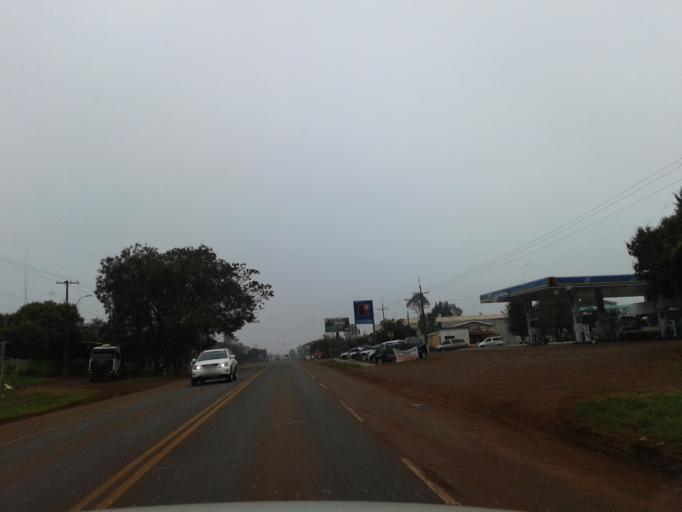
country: PY
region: Alto Parana
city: Colonia Yguazu
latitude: -25.5032
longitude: -54.8988
